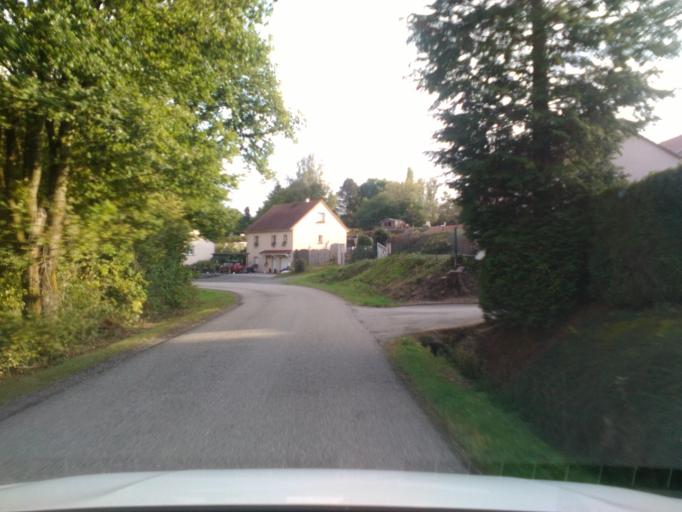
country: FR
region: Lorraine
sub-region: Departement des Vosges
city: Ban-de-Laveline
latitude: 48.3124
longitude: 7.0822
